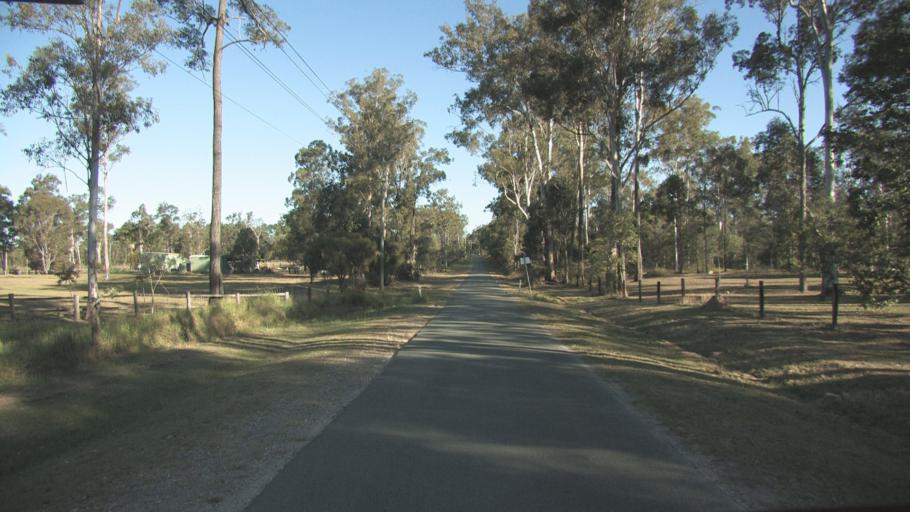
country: AU
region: Queensland
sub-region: Logan
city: North Maclean
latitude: -27.7836
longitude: 153.0459
